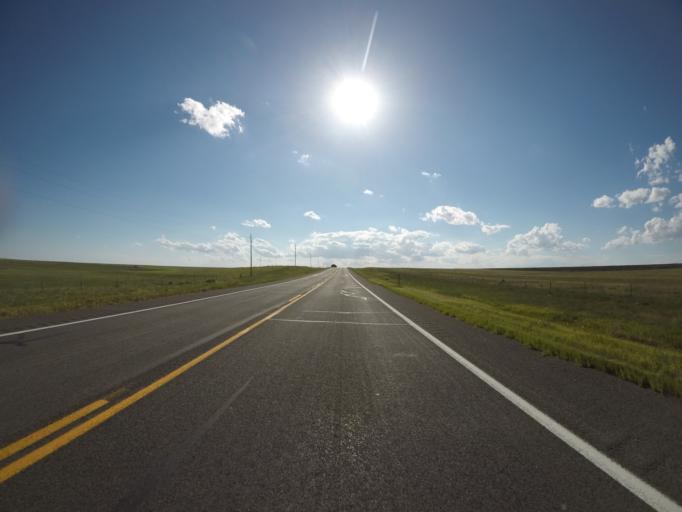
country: US
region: Colorado
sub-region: Morgan County
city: Fort Morgan
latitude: 40.6113
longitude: -103.8131
